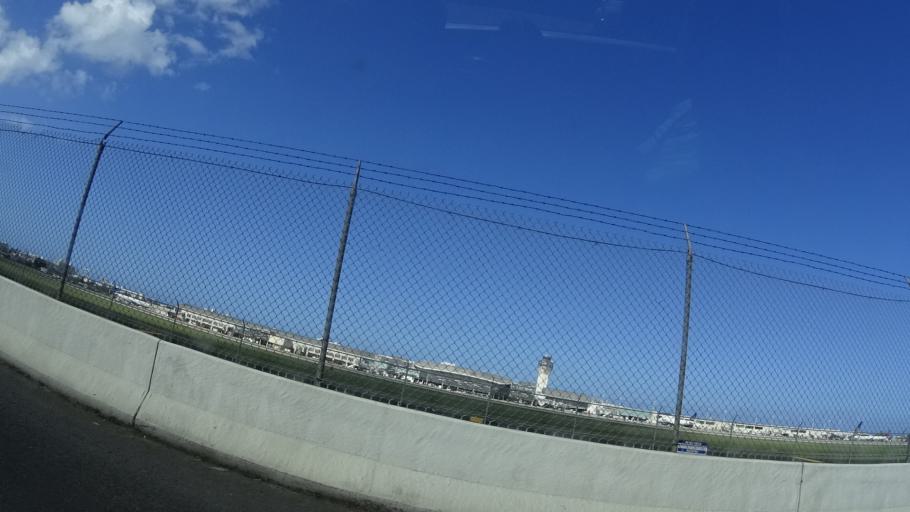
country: PR
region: Carolina
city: Carolina
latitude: 18.4320
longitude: -66.0046
